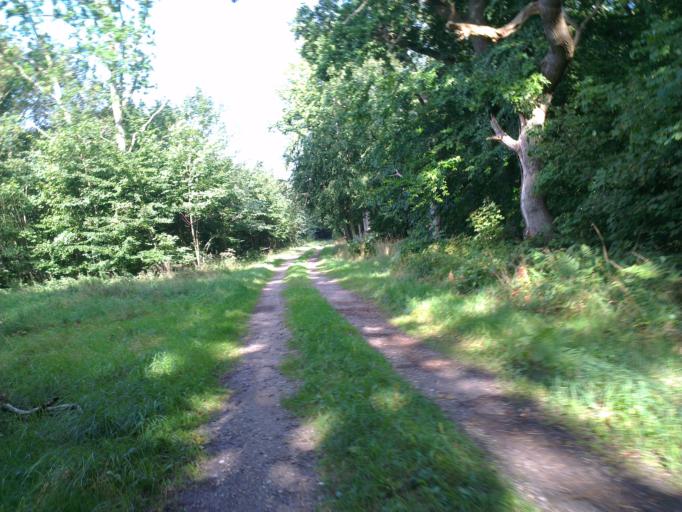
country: DK
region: Capital Region
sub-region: Frederikssund Kommune
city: Jaegerspris
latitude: 55.8903
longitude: 11.9978
